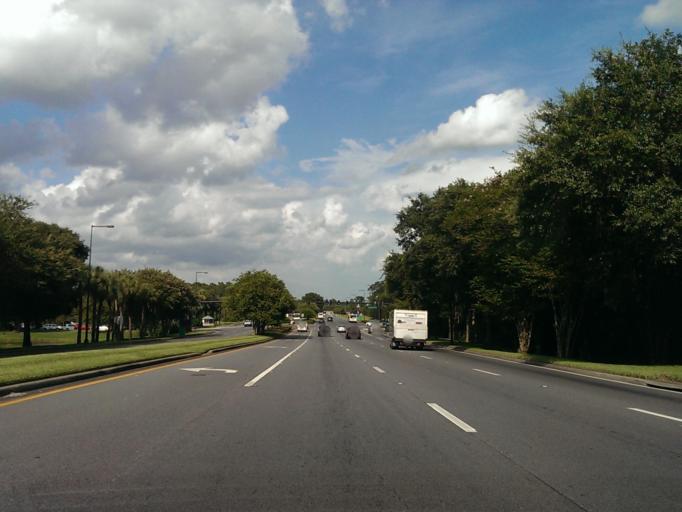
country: US
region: Florida
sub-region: Osceola County
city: Celebration
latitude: 28.3625
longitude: -81.5548
